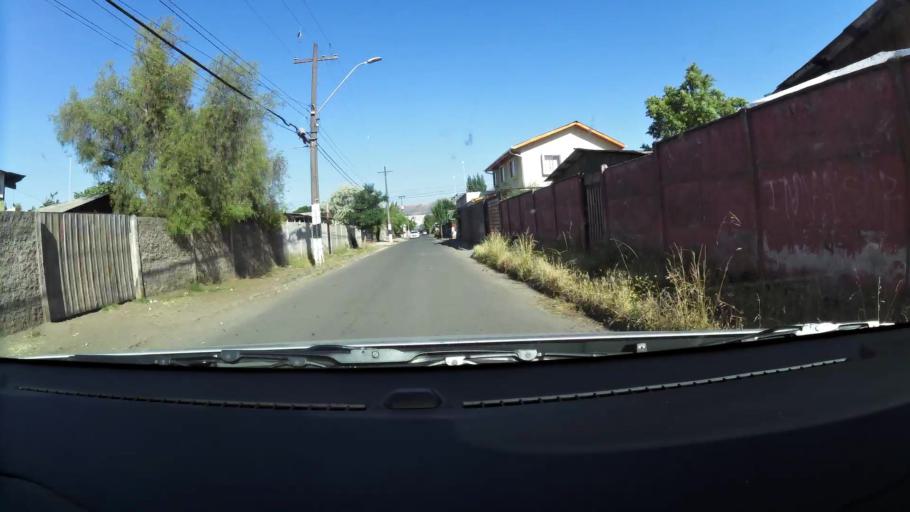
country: CL
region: Santiago Metropolitan
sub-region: Provincia de Maipo
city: San Bernardo
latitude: -33.6149
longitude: -70.6920
